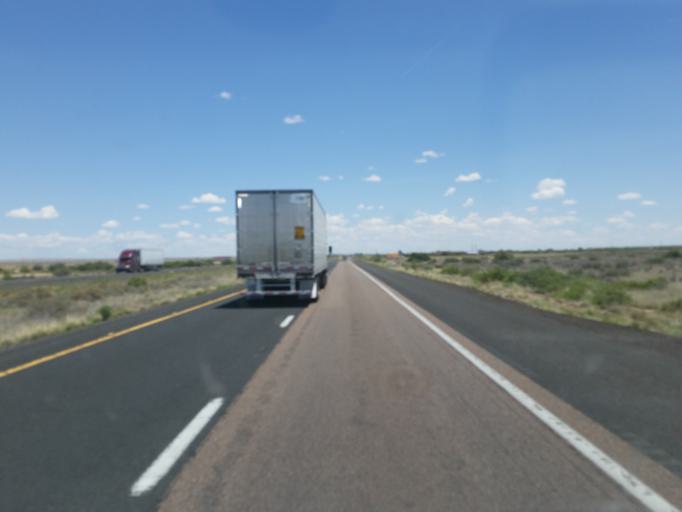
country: US
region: Arizona
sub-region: Navajo County
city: Joseph City
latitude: 34.9701
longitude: -110.4489
